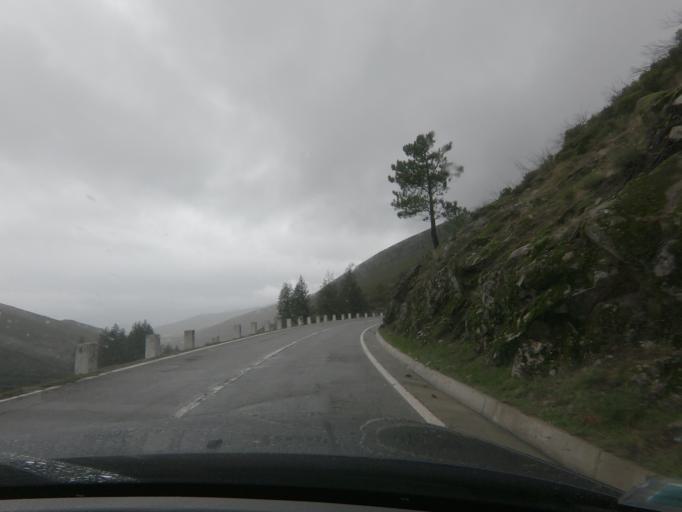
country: PT
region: Vila Real
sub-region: Mondim de Basto
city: Mondim de Basto
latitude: 41.3371
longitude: -7.8645
